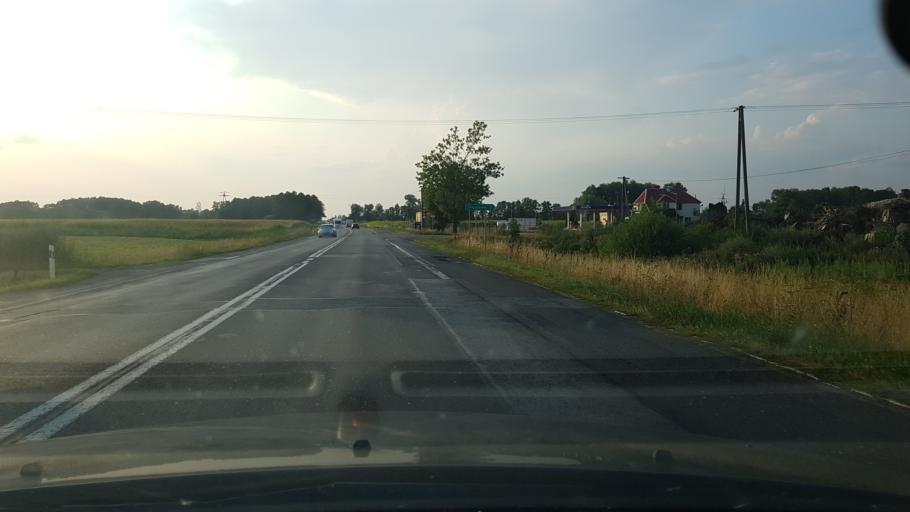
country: PL
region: Masovian Voivodeship
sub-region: Powiat plonski
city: Plonsk
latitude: 52.6771
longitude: 20.3691
